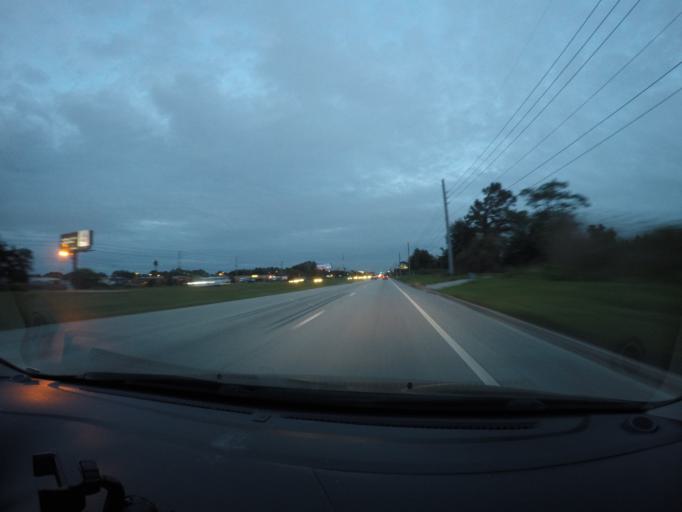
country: US
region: Florida
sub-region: Orange County
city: Tangelo Park
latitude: 28.4499
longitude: -81.4499
